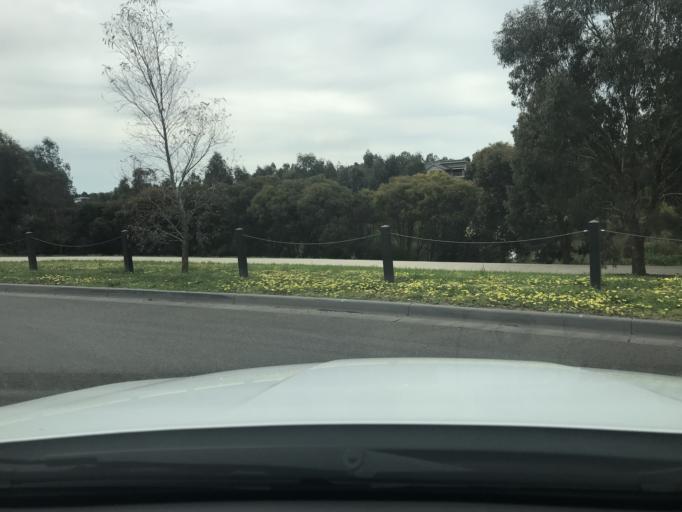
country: AU
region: Victoria
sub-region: Hume
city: Roxburgh Park
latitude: -37.5973
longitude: 144.9054
